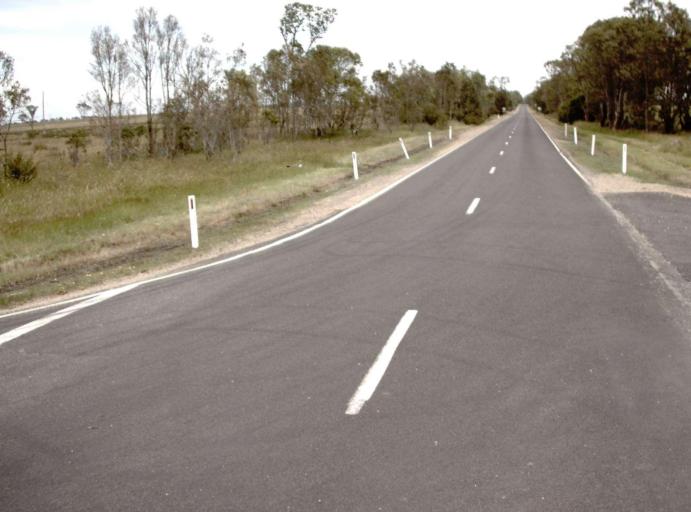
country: AU
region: Victoria
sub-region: Wellington
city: Sale
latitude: -37.9898
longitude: 147.1935
